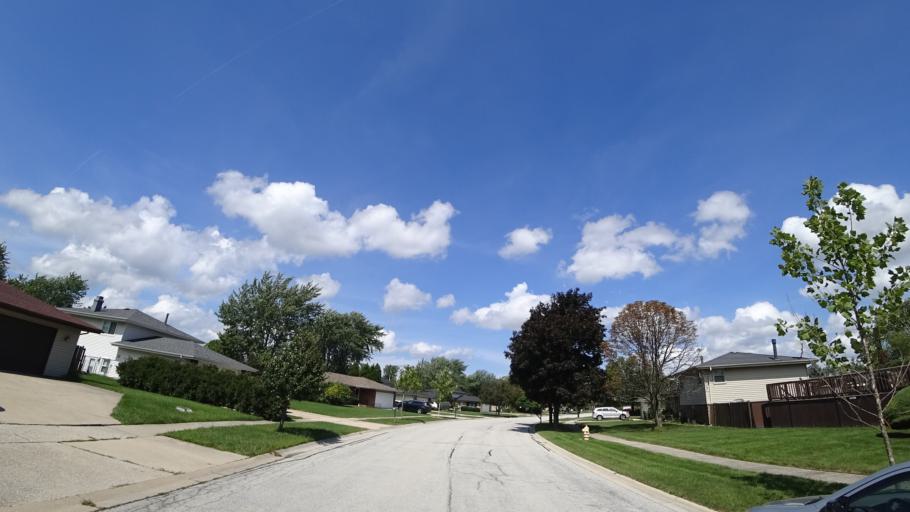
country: US
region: Illinois
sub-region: Cook County
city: Tinley Park
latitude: 41.5644
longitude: -87.7784
